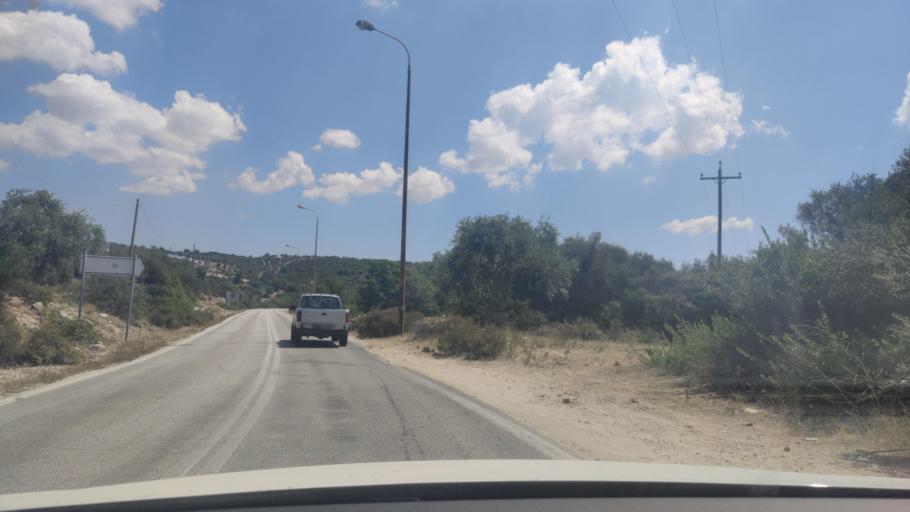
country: GR
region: East Macedonia and Thrace
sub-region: Nomos Kavalas
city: Limenaria
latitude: 40.6393
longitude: 24.5234
